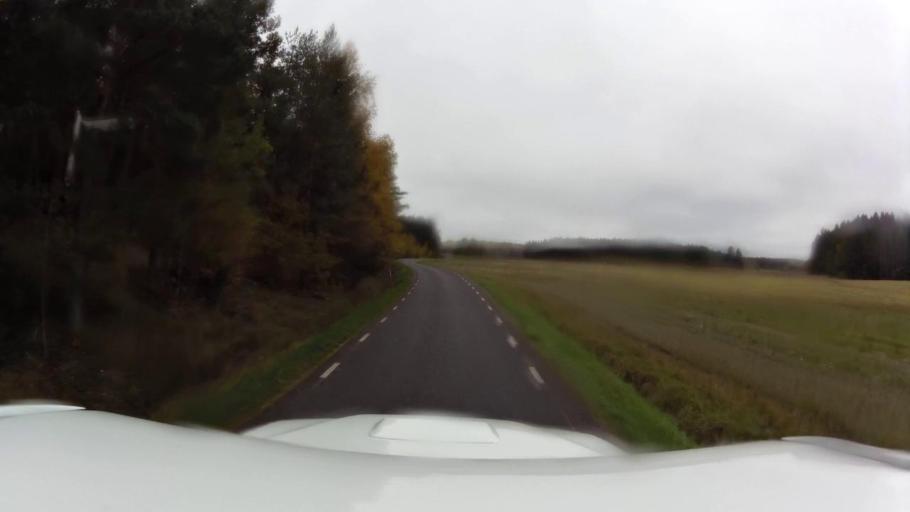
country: SE
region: OEstergoetland
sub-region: Linkopings Kommun
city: Linghem
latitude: 58.4672
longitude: 15.7857
